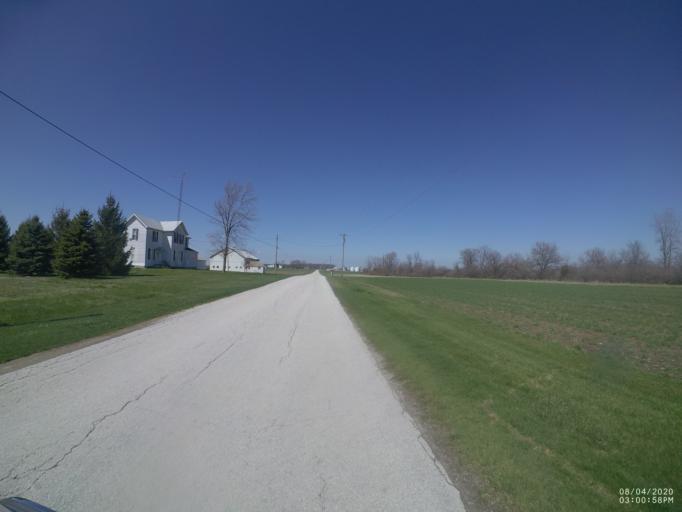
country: US
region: Ohio
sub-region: Sandusky County
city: Stony Prairie
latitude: 41.3303
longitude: -83.2397
